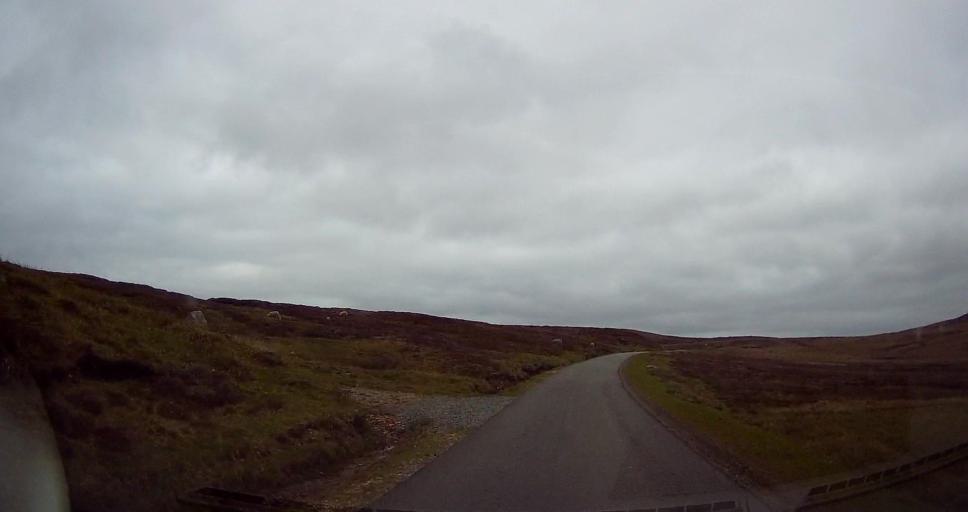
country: GB
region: Scotland
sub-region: Shetland Islands
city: Lerwick
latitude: 60.3150
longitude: -1.3419
